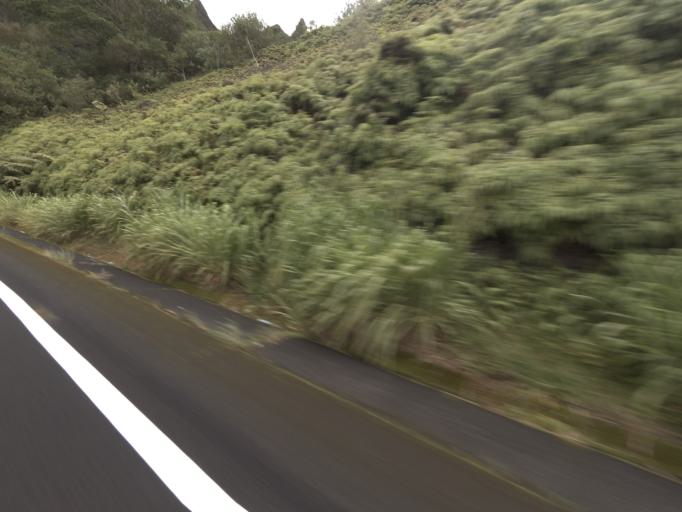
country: US
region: Hawaii
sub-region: Honolulu County
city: Kane'ohe
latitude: 21.3844
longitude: -157.8151
